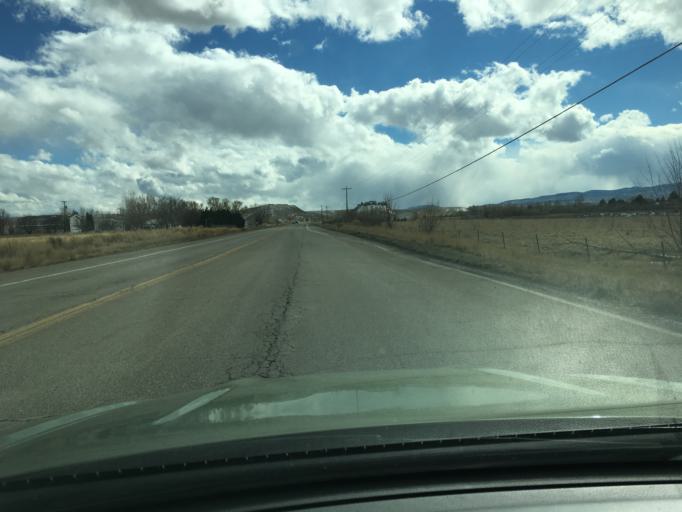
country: US
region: Colorado
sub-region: Mesa County
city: Clifton
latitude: 39.0328
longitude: -108.4595
